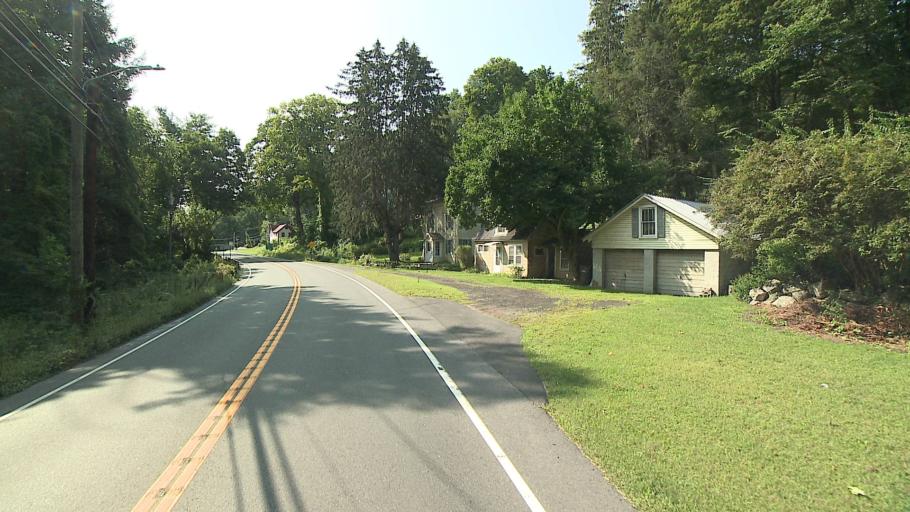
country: US
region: Connecticut
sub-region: Fairfield County
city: Sherman
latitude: 41.5966
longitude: -73.4580
